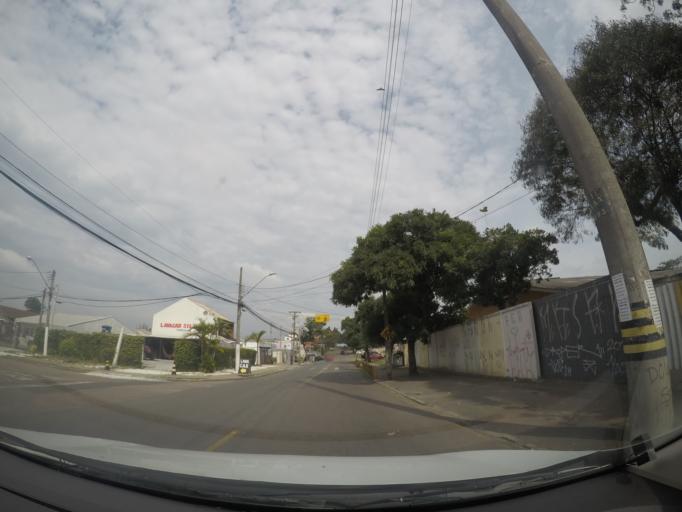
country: BR
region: Parana
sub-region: Sao Jose Dos Pinhais
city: Sao Jose dos Pinhais
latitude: -25.5177
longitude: -49.2766
